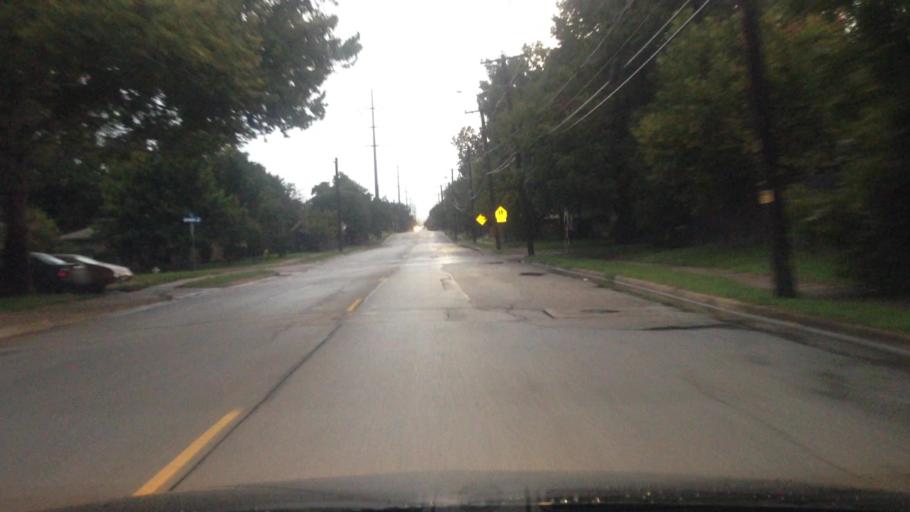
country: US
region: Texas
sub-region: Tarrant County
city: Arlington
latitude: 32.7319
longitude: -97.0716
